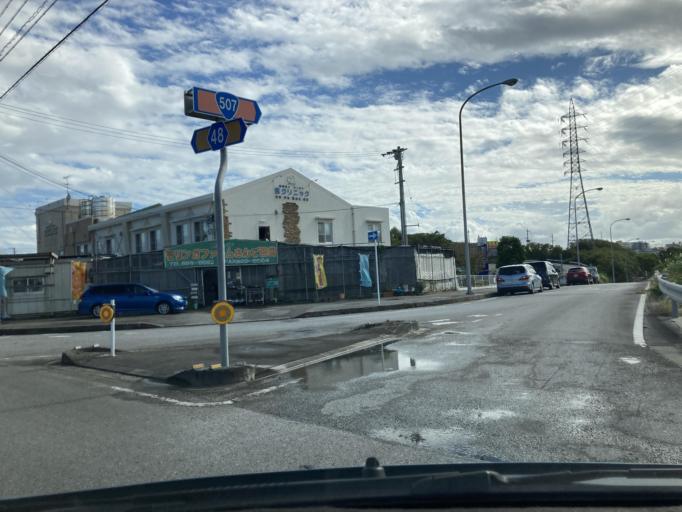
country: JP
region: Okinawa
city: Tomigusuku
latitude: 26.1733
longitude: 127.7274
